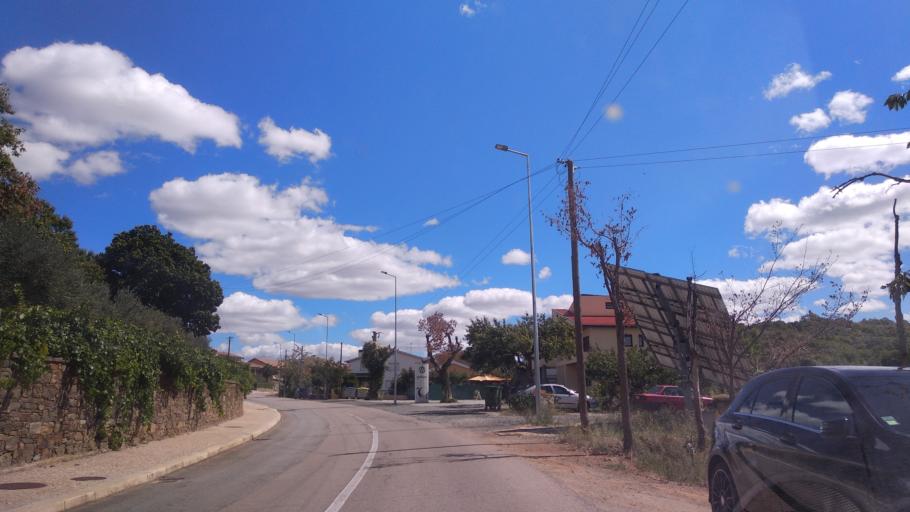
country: PT
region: Braganca
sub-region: Braganca Municipality
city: Braganca
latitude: 41.7865
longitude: -6.7682
